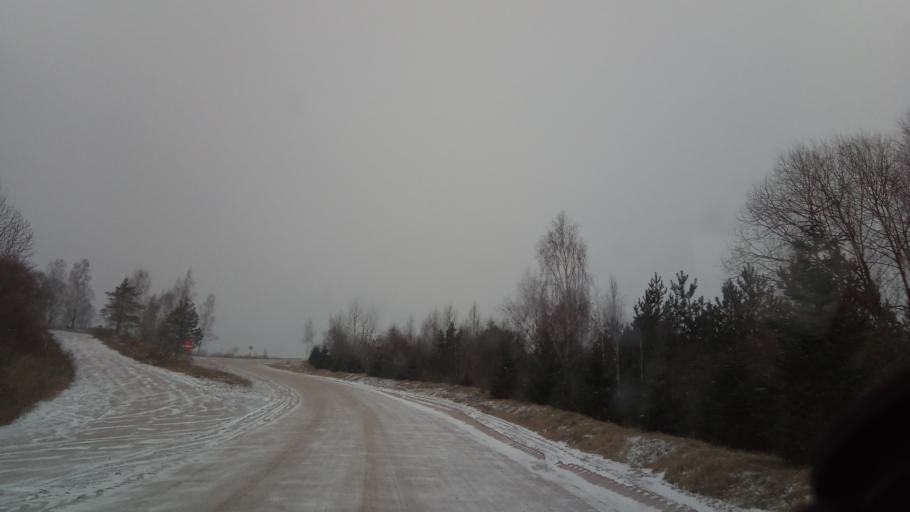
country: LT
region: Vilnius County
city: Ukmerge
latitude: 55.3314
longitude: 24.8830
